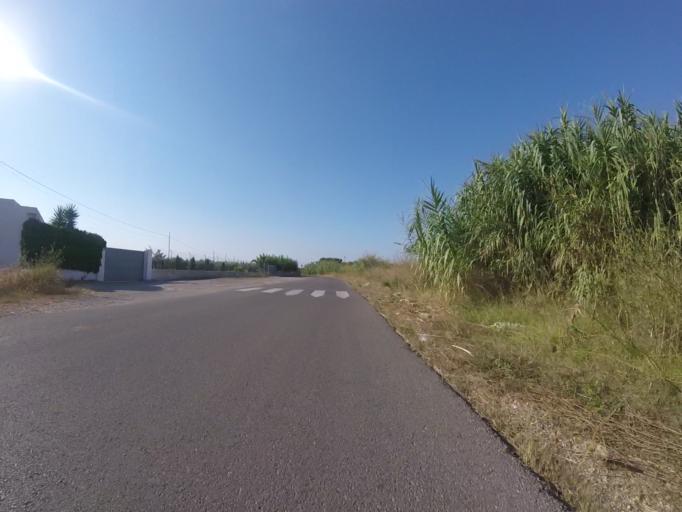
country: ES
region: Valencia
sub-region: Provincia de Castello
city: Benicarlo
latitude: 40.4226
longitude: 0.4347
